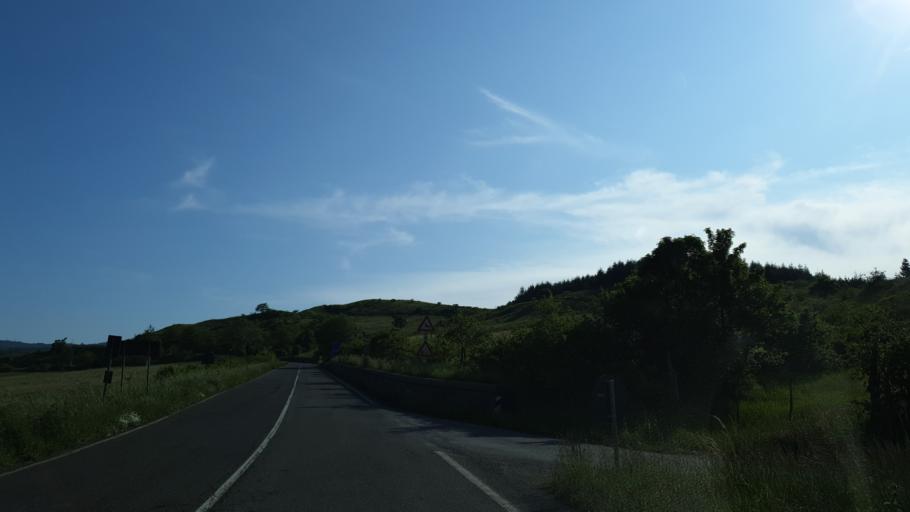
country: IT
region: Tuscany
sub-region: Province of Arezzo
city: Montemignaio
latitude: 43.7880
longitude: 11.6224
